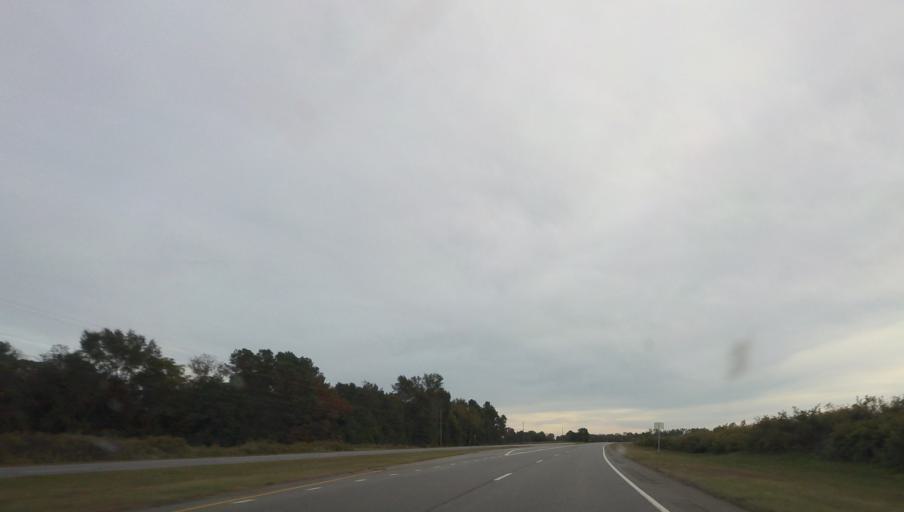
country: US
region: Georgia
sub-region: Houston County
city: Perry
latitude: 32.4613
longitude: -83.6947
